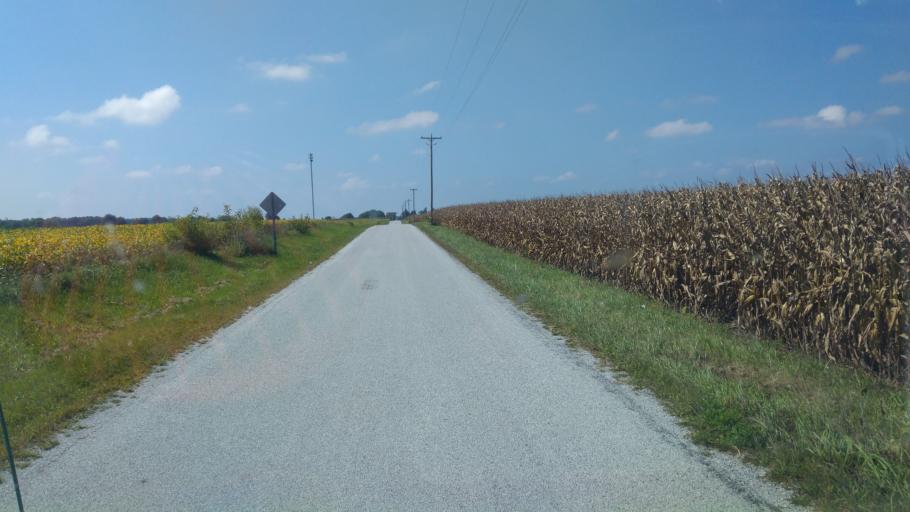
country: US
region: Ohio
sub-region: Hardin County
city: Kenton
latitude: 40.6742
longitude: -83.5981
